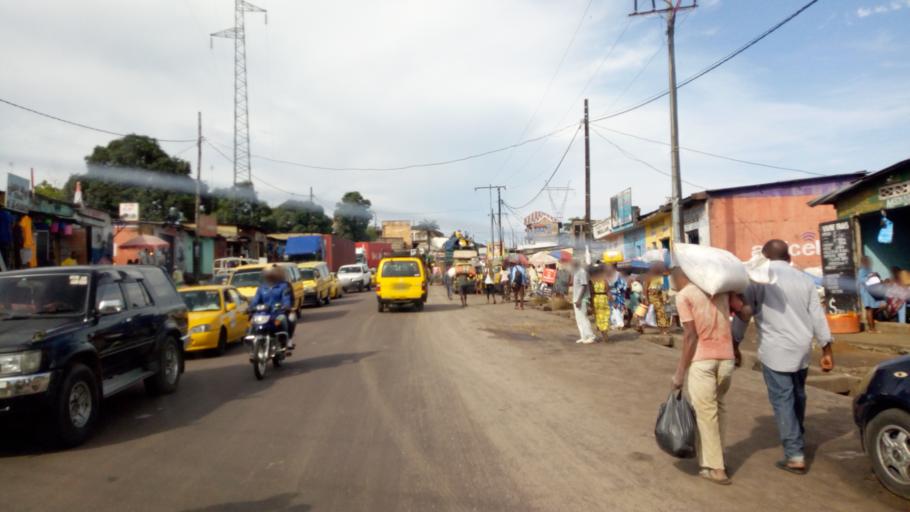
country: CD
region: Kinshasa
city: Kinshasa
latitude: -4.4464
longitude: 15.2505
